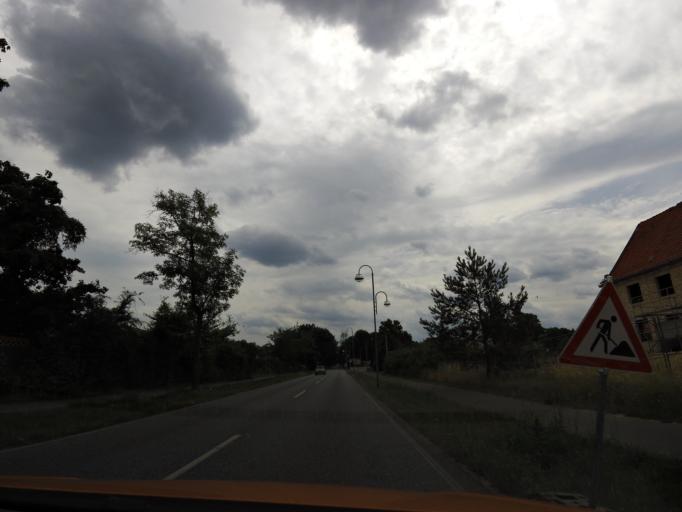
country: DE
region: Brandenburg
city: Zossen
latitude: 52.1967
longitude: 13.4592
